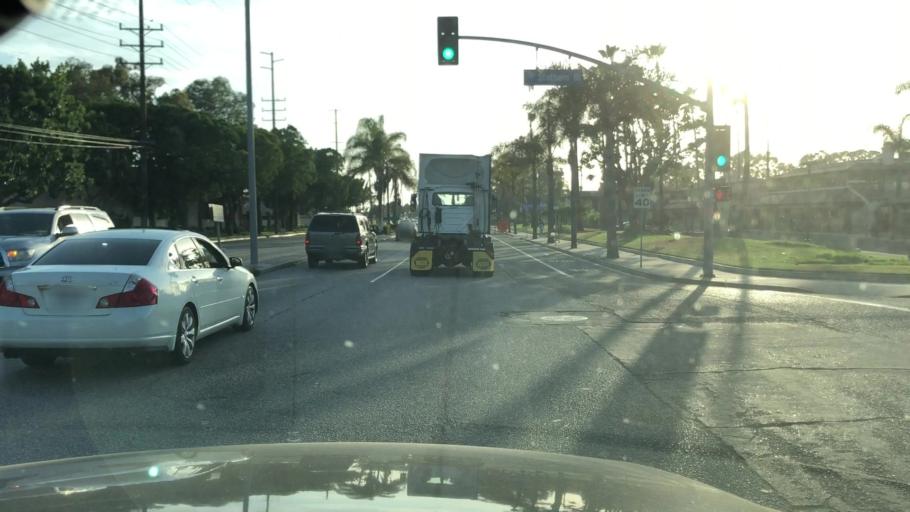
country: US
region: California
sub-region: Ventura County
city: Oxnard
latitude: 34.1734
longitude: -119.1656
